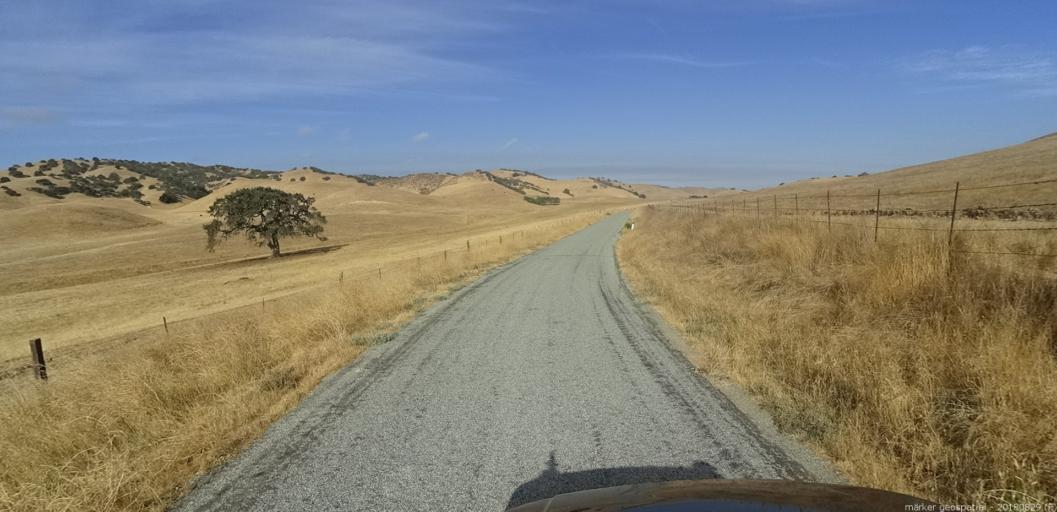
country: US
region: California
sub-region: Monterey County
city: King City
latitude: 36.0267
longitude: -120.9521
